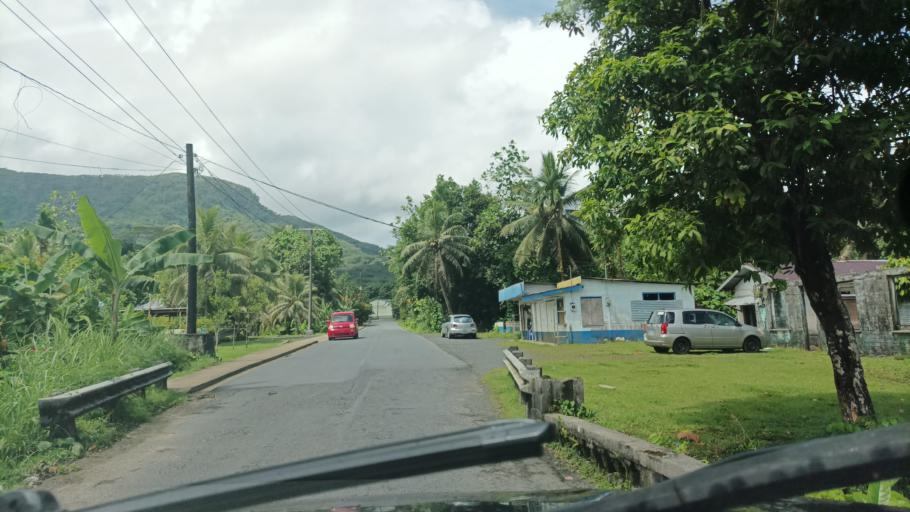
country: FM
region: Pohnpei
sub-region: Sokehs Municipality
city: Palikir - National Government Center
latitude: 6.9388
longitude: 158.1841
